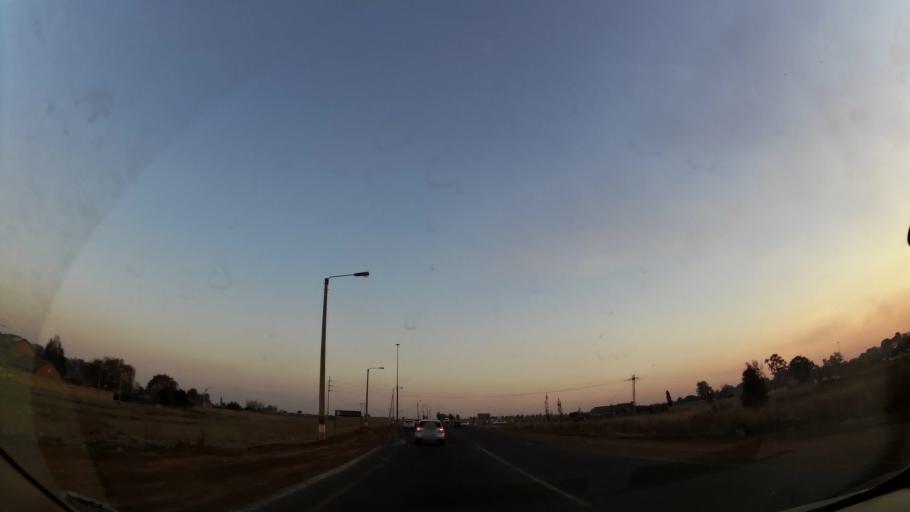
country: ZA
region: Gauteng
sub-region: Ekurhuleni Metropolitan Municipality
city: Springs
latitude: -26.3468
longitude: 28.4154
